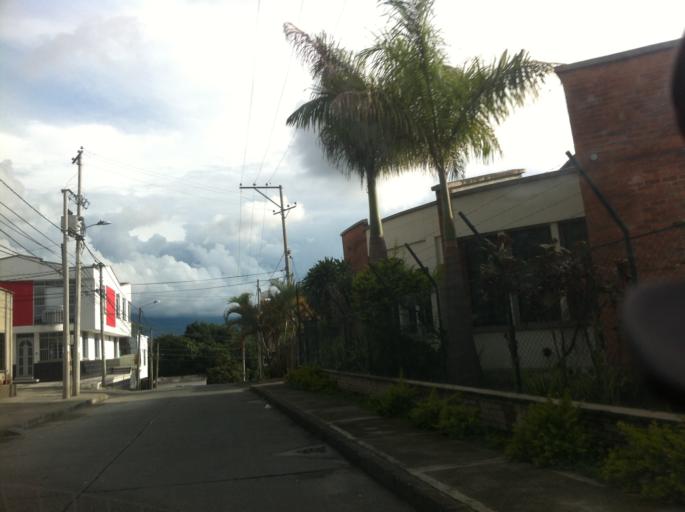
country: CO
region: Quindio
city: Armenia
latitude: 4.5357
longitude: -75.6835
